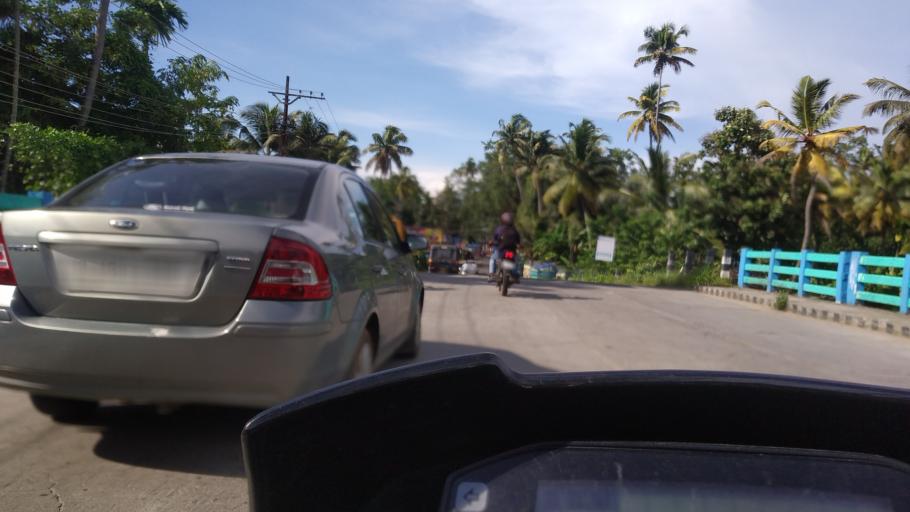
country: IN
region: Kerala
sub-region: Ernakulam
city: Elur
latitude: 10.0548
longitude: 76.2155
